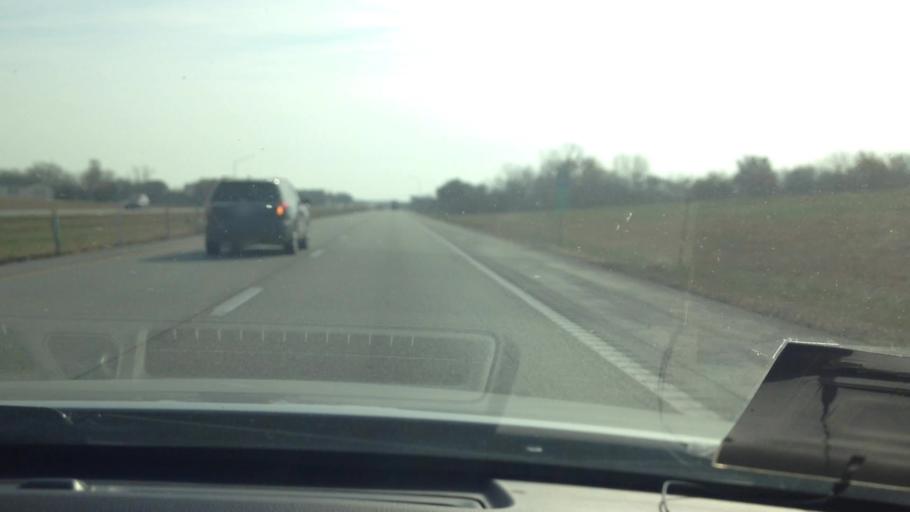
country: US
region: Missouri
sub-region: Cass County
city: Peculiar
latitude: 38.7225
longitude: -94.4546
